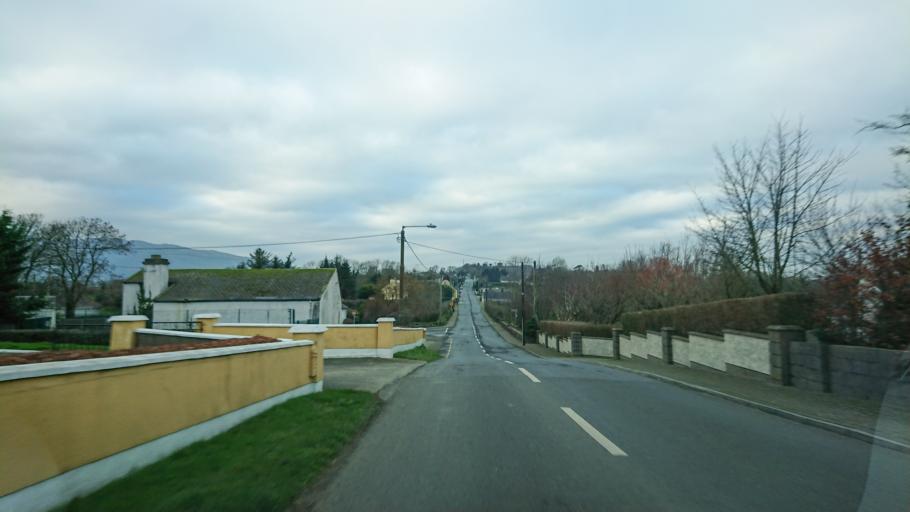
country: IE
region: Munster
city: Carrick-on-Suir
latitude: 52.3042
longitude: -7.4923
